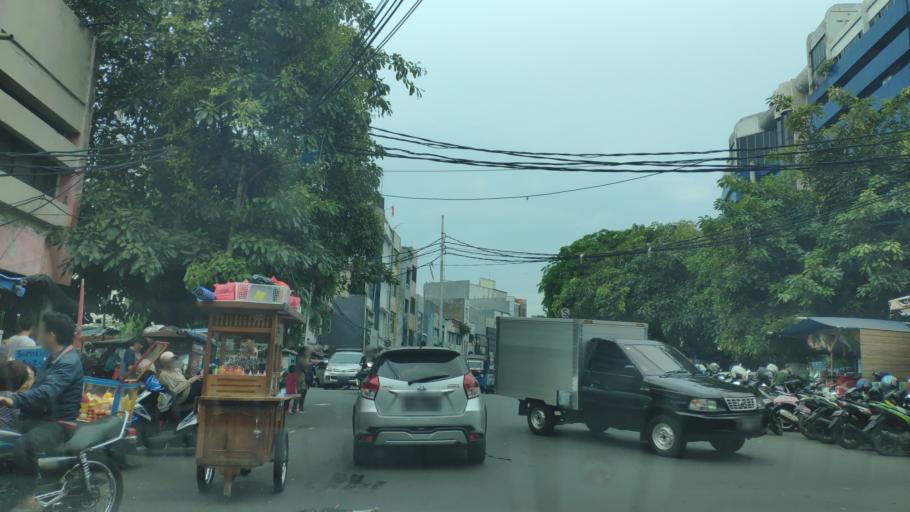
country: ID
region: Jakarta Raya
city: Jakarta
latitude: -6.1412
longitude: 106.8125
